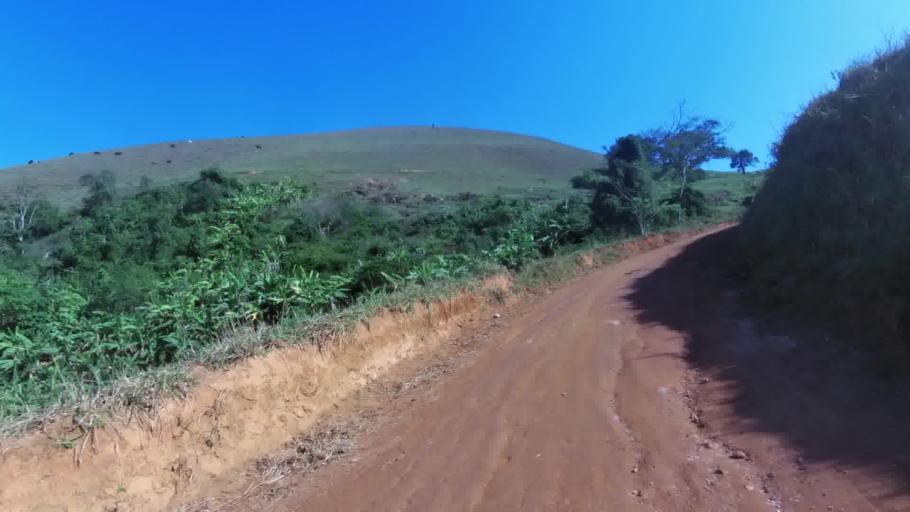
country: BR
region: Espirito Santo
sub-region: Alfredo Chaves
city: Alfredo Chaves
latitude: -20.6822
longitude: -40.7813
